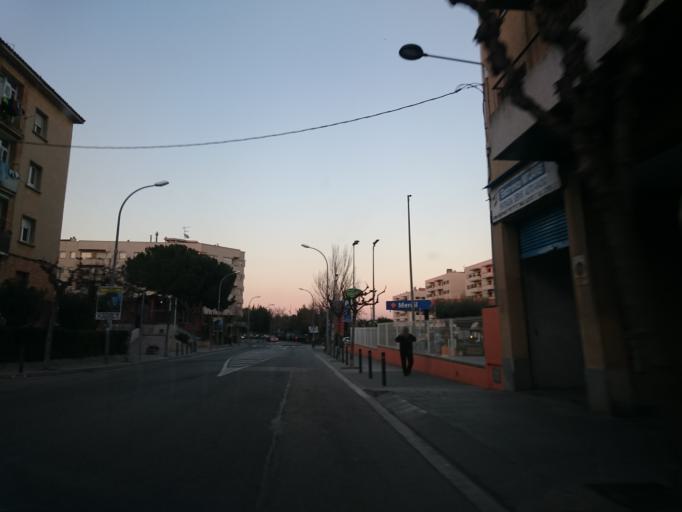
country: ES
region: Catalonia
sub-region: Provincia de Barcelona
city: Vilafranca del Penedes
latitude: 41.3502
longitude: 1.7049
